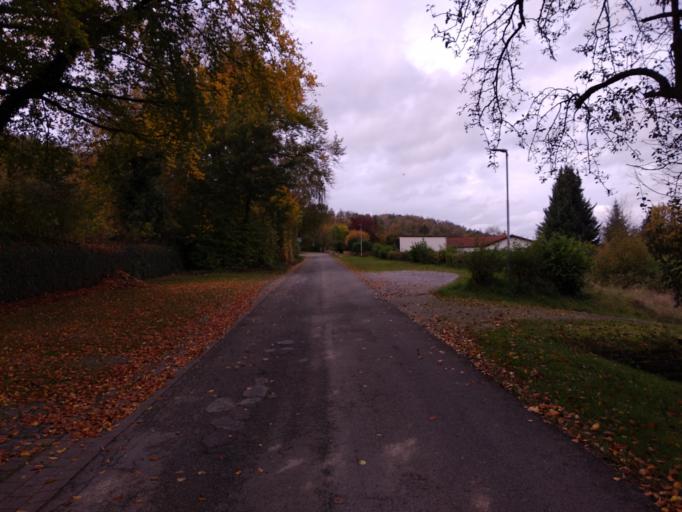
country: DE
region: North Rhine-Westphalia
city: Beverungen
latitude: 51.6707
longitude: 9.3650
